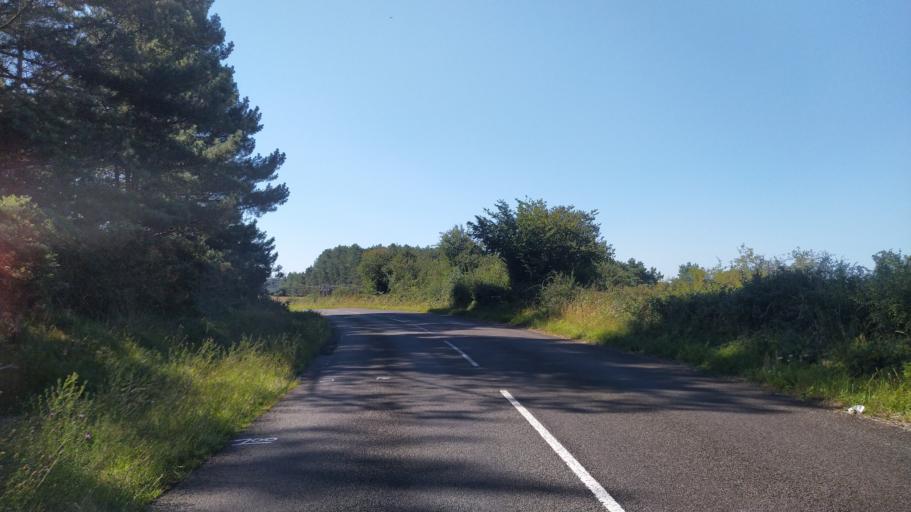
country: GB
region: England
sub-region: Dorset
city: Wareham
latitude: 50.7274
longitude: -2.1178
